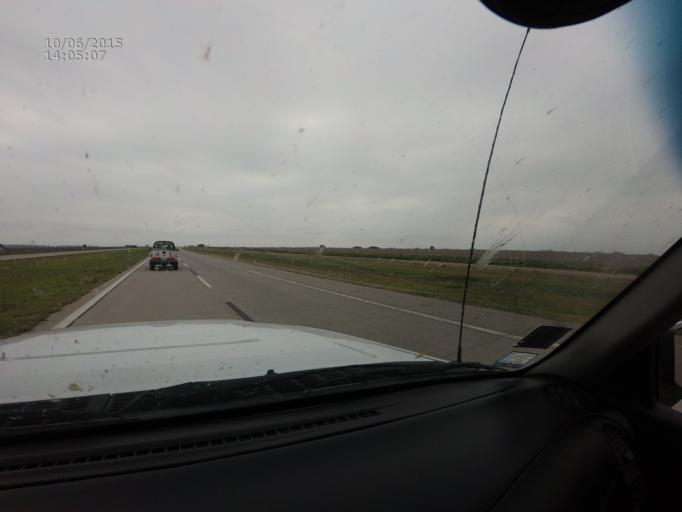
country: AR
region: Cordoba
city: Morrison
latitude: -32.5137
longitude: -62.9876
